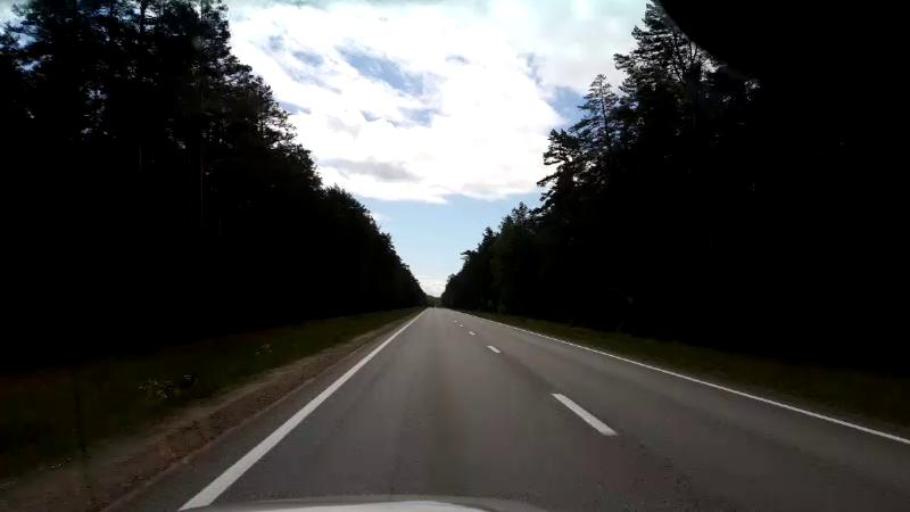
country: LV
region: Salacgrivas
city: Salacgriva
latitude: 57.5162
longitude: 24.4307
